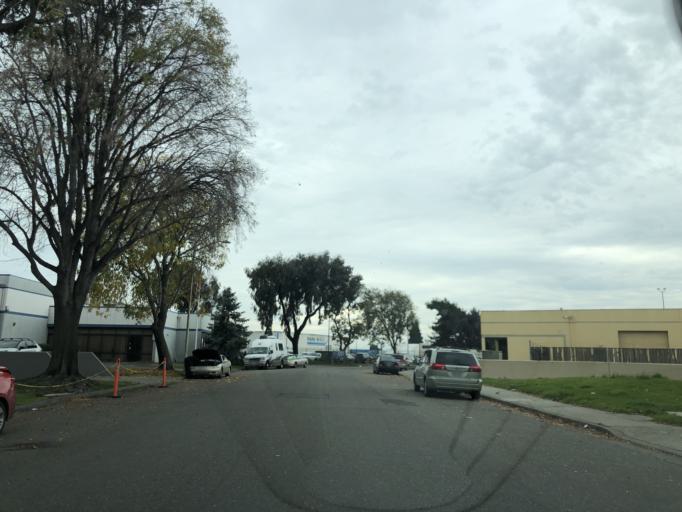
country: US
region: California
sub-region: Alameda County
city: San Leandro
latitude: 37.7270
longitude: -122.1955
